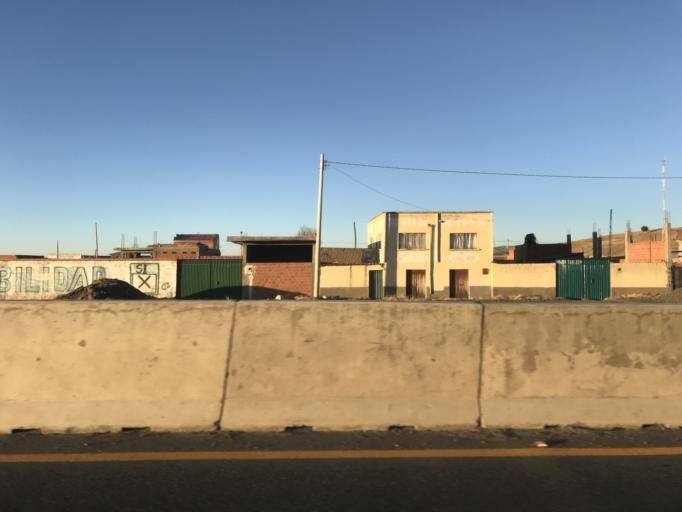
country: BO
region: La Paz
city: Batallas
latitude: -16.2983
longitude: -68.5237
